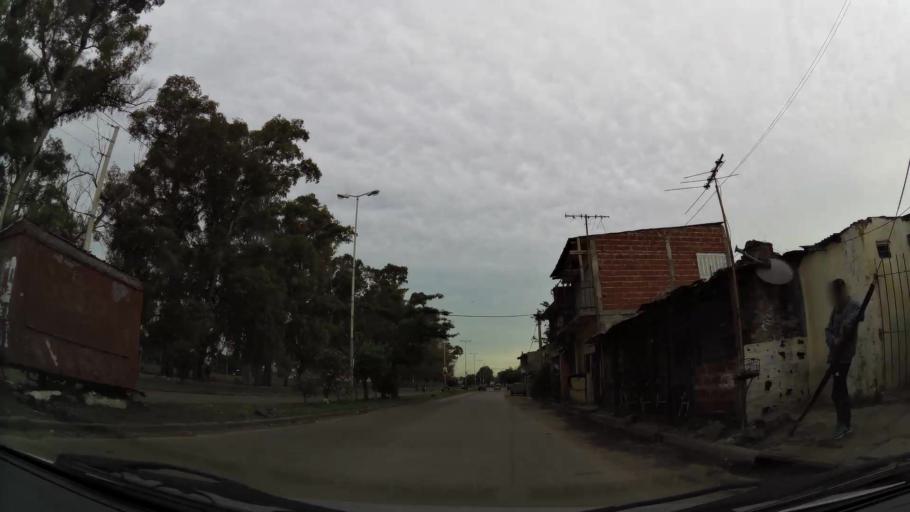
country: AR
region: Buenos Aires
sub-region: Partido de Lanus
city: Lanus
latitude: -34.7239
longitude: -58.3481
